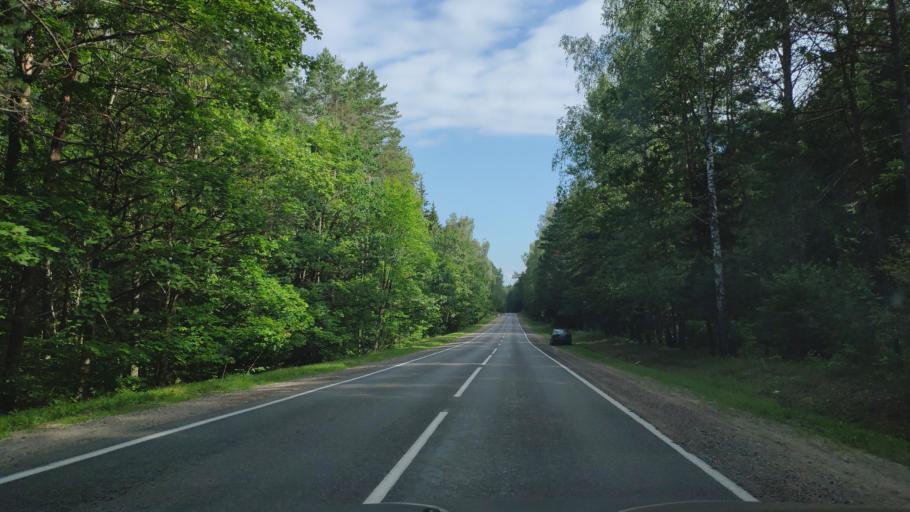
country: BY
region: Minsk
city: Novosel'ye
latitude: 53.9468
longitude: 27.2453
